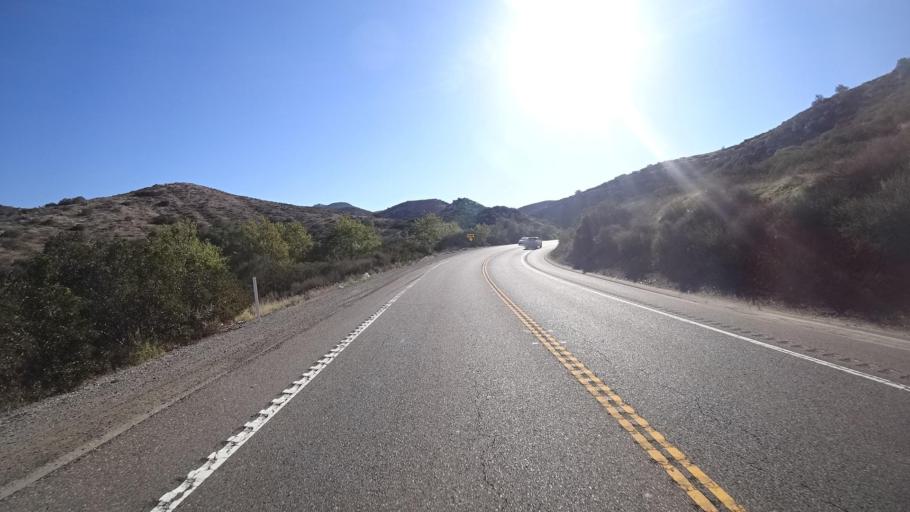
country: US
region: California
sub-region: San Diego County
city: Jamul
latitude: 32.6542
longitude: -116.7930
